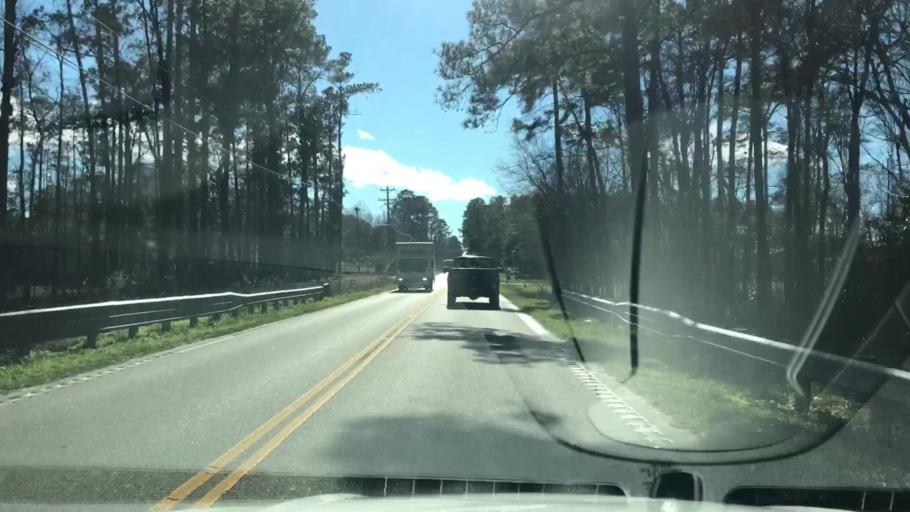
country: US
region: South Carolina
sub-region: Dorchester County
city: Summerville
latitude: 33.0521
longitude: -80.2413
